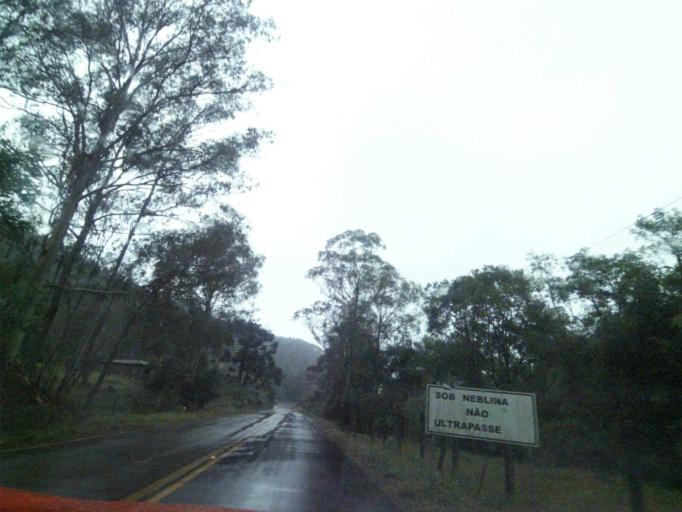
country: BR
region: Santa Catarina
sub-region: Anitapolis
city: Anitapolis
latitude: -27.8110
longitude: -49.0470
